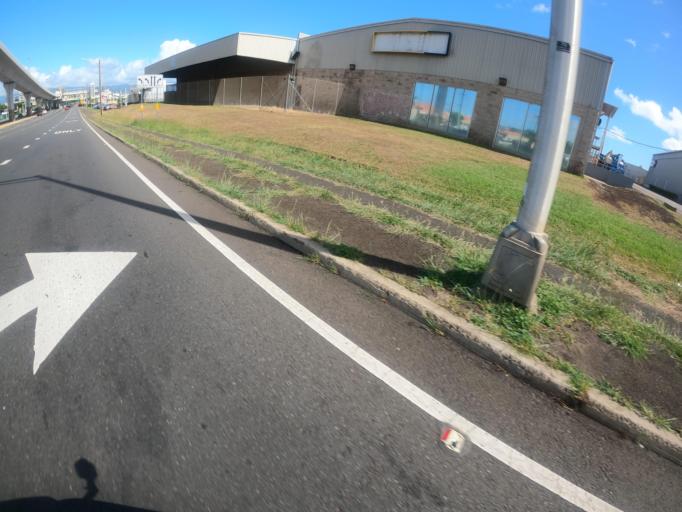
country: US
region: Hawaii
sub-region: Honolulu County
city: Royal Kunia
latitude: 21.3769
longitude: -158.0250
